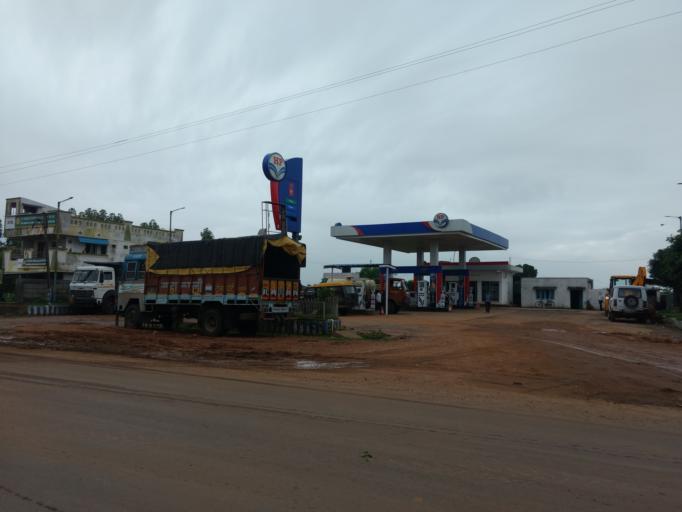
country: IN
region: Maharashtra
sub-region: Chandrapur
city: Mul
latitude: 19.9413
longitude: 79.8940
